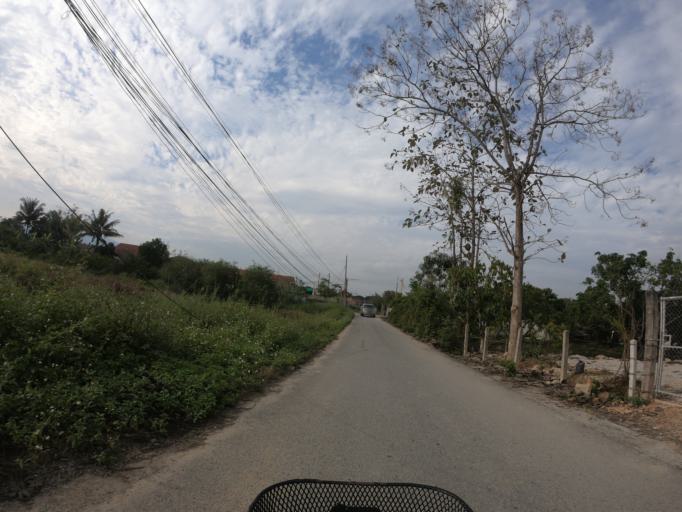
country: TH
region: Chiang Mai
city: San Sai
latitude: 18.7995
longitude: 99.0509
